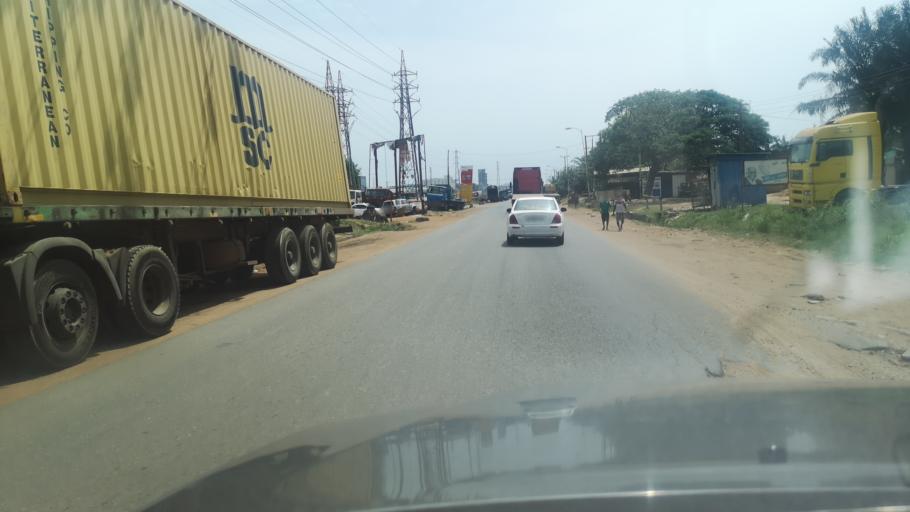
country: GH
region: Greater Accra
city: Tema
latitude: 5.6303
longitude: -0.0072
